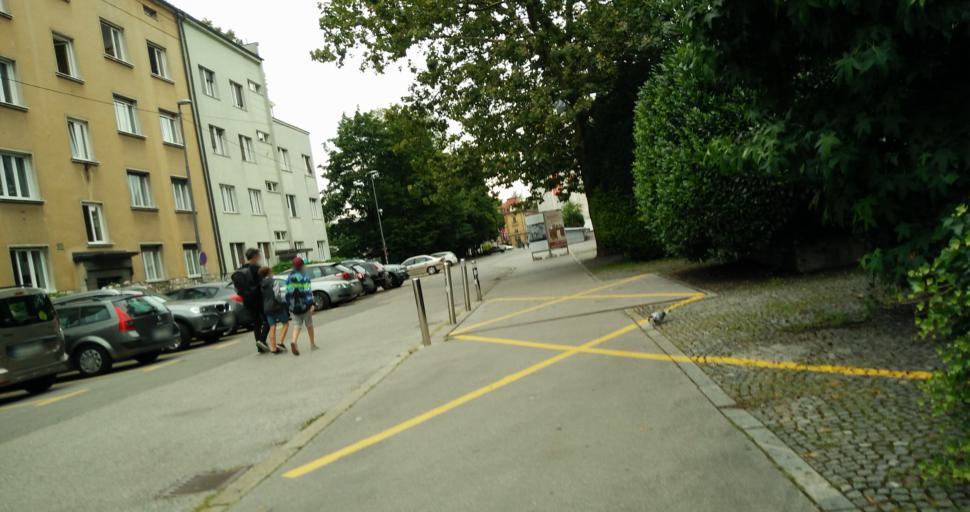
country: SI
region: Ljubljana
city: Ljubljana
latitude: 46.0494
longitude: 14.5010
